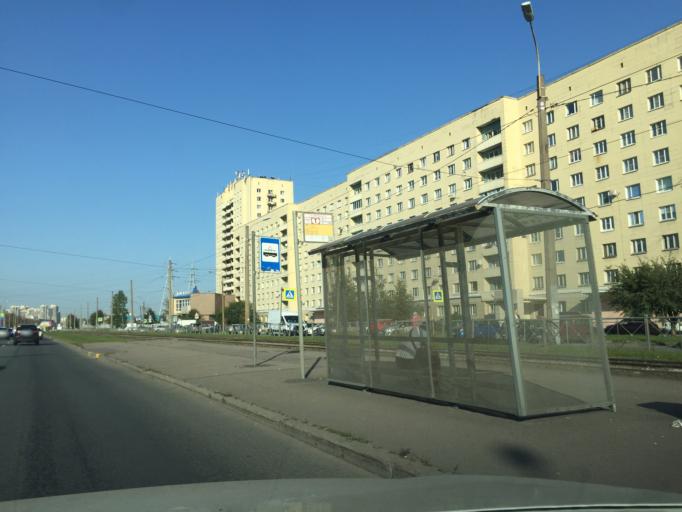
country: RU
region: St.-Petersburg
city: Grazhdanka
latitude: 60.0123
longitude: 30.4342
